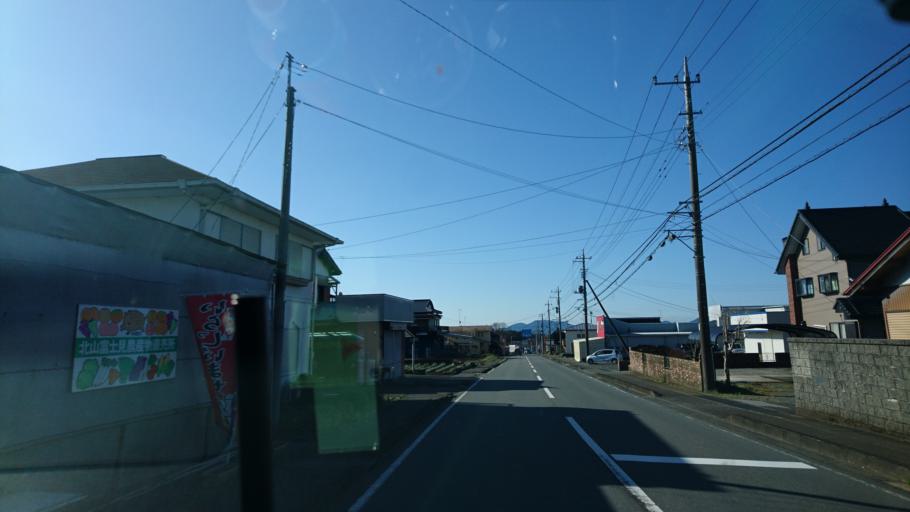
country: JP
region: Shizuoka
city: Fujinomiya
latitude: 35.2782
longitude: 138.6048
